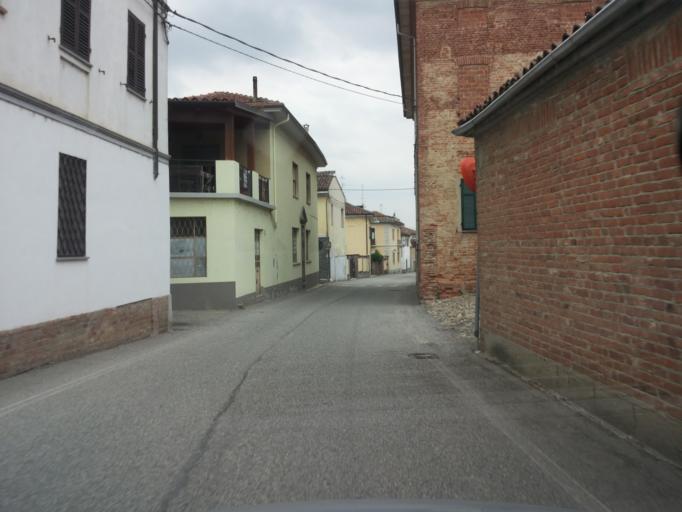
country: IT
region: Piedmont
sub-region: Provincia di Alessandria
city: Mirabello Monferrato
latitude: 45.0341
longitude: 8.5234
